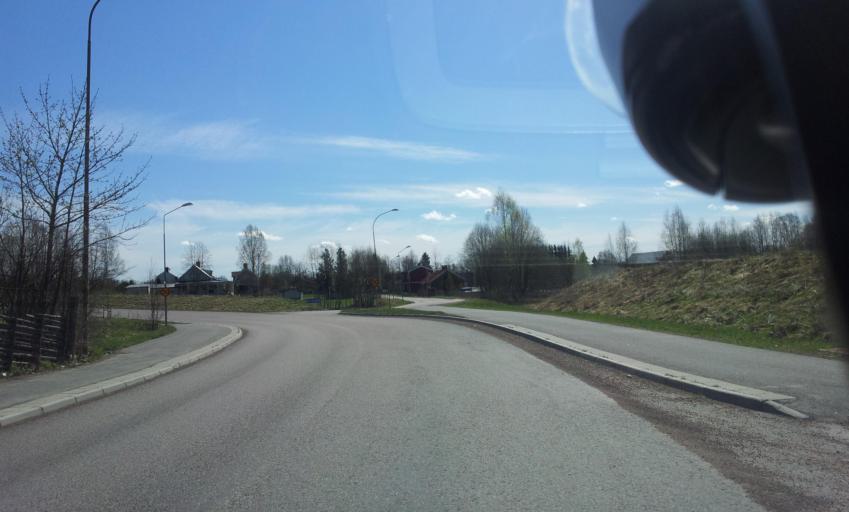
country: SE
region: Dalarna
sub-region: Borlange Kommun
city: Borlaenge
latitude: 60.4837
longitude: 15.4659
